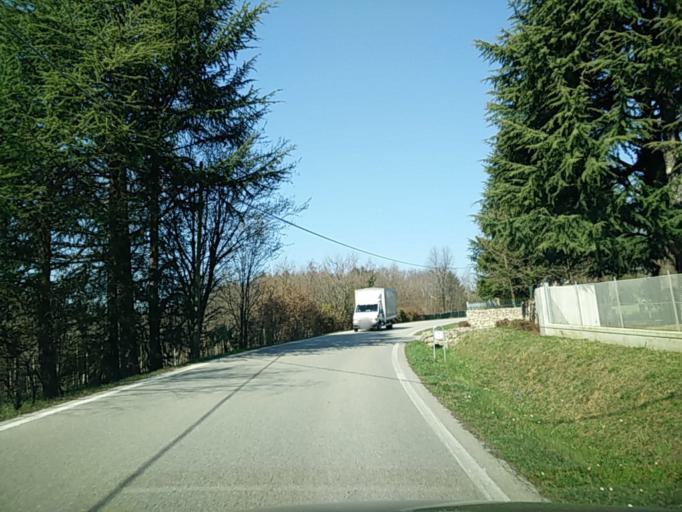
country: IT
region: Veneto
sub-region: Provincia di Treviso
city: Nervesa della Battaglia
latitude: 45.8365
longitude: 12.1889
